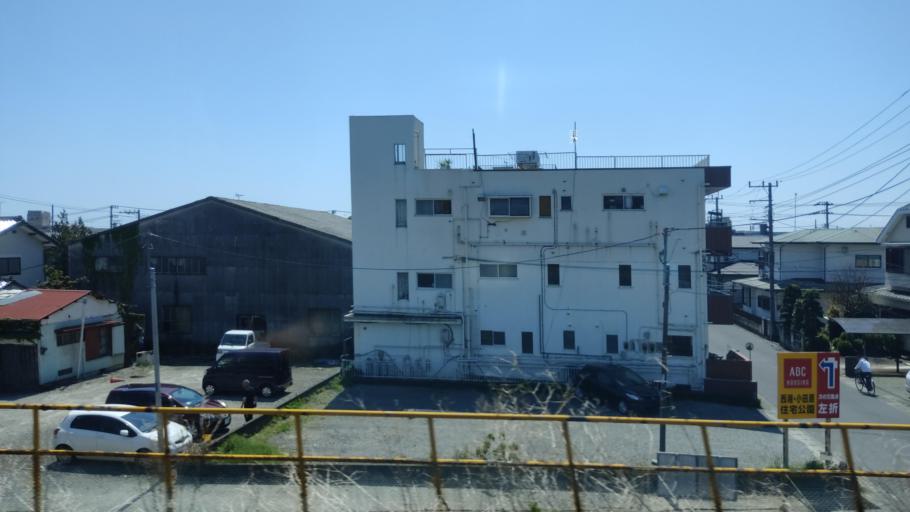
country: JP
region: Kanagawa
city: Odawara
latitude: 35.2787
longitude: 139.1989
